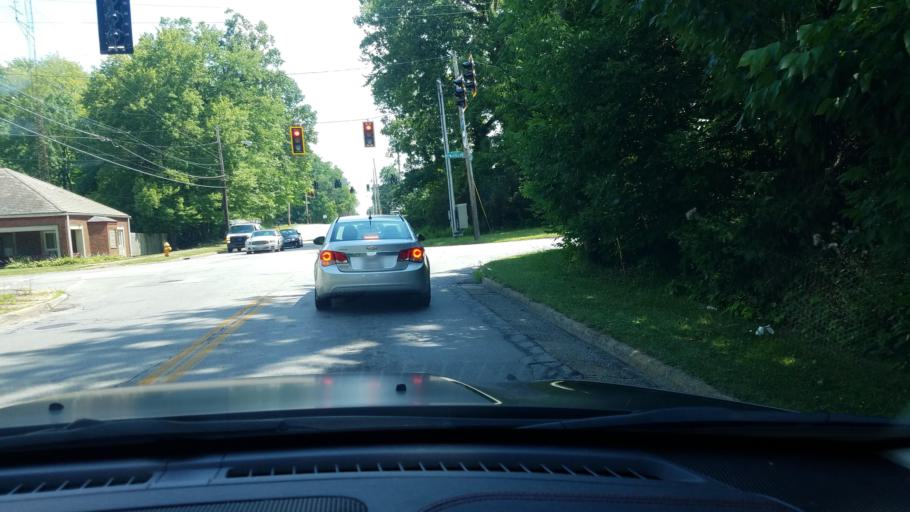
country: US
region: Ohio
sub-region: Mahoning County
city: Youngstown
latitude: 41.0870
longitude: -80.6999
